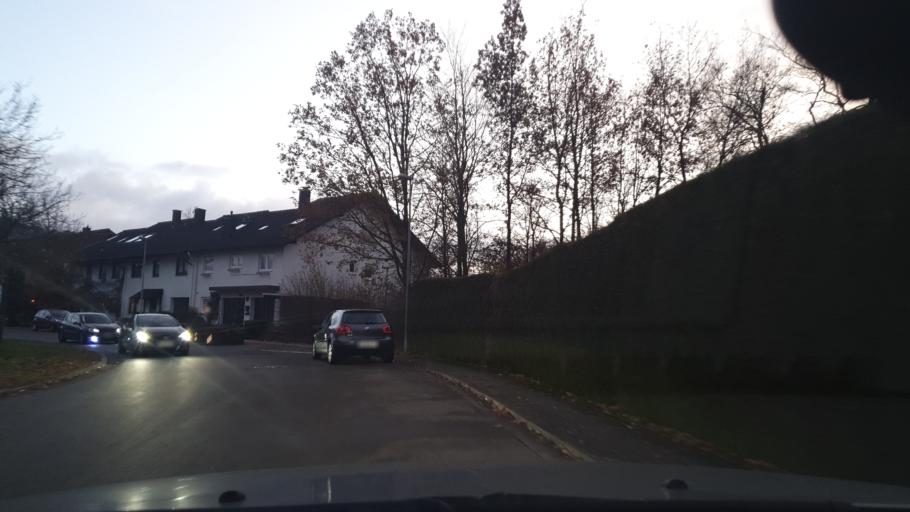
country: DE
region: Rheinland-Pfalz
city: Stelzenberg
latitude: 49.4214
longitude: 7.7364
